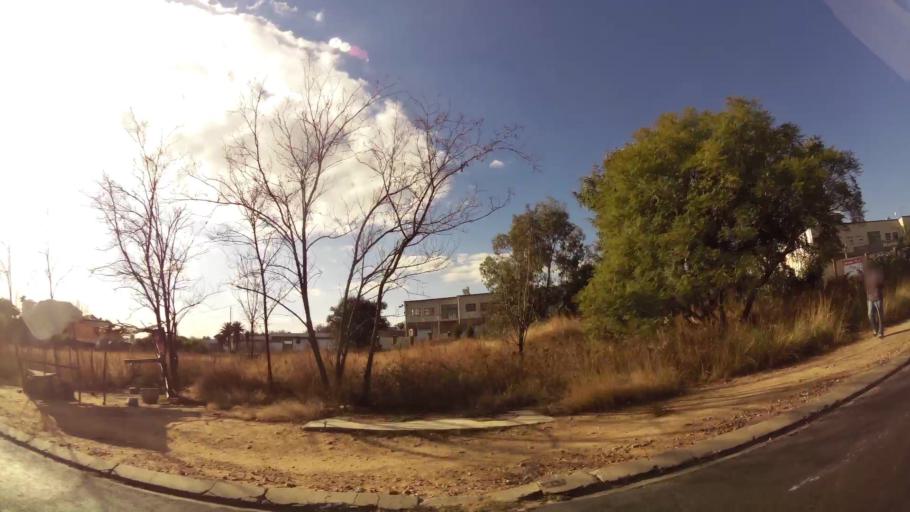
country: ZA
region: Gauteng
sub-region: City of Johannesburg Metropolitan Municipality
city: Midrand
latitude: -26.0082
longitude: 28.1296
